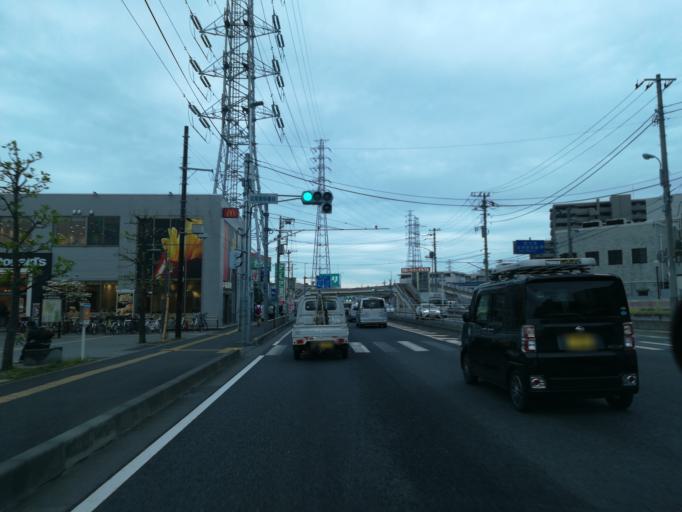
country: JP
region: Saitama
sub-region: Kawaguchi-shi
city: Hatogaya-honcho
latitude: 35.8304
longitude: 139.7364
